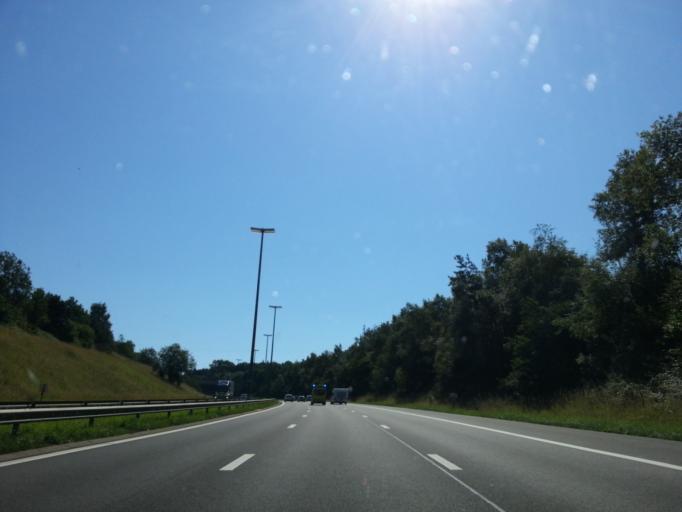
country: BE
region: Wallonia
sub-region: Province de Liege
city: Spa
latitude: 50.5262
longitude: 5.8847
